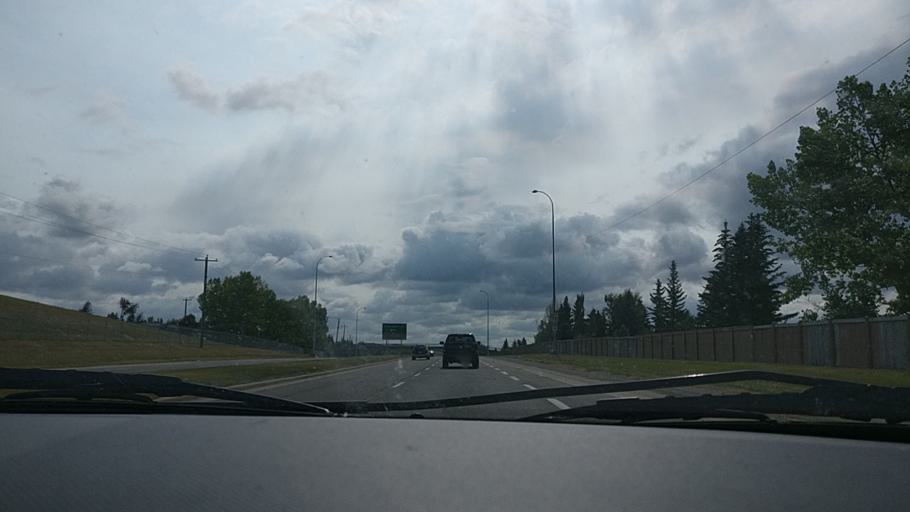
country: CA
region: Alberta
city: Calgary
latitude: 51.1139
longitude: -114.1521
